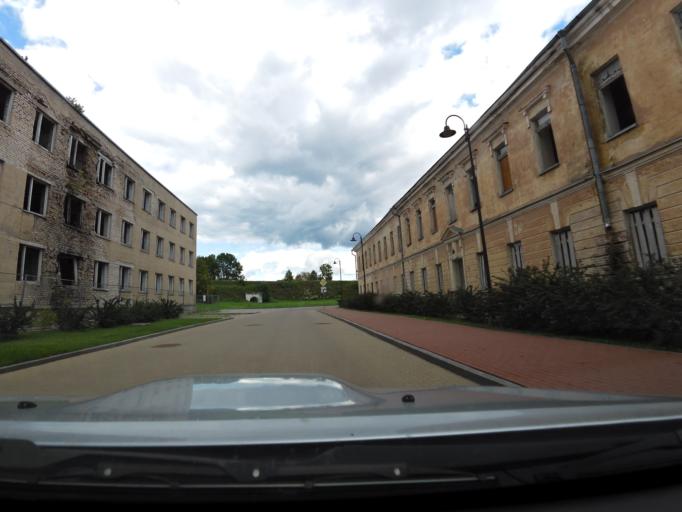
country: LV
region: Daugavpils
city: Daugavpils
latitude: 55.8881
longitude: 26.4927
